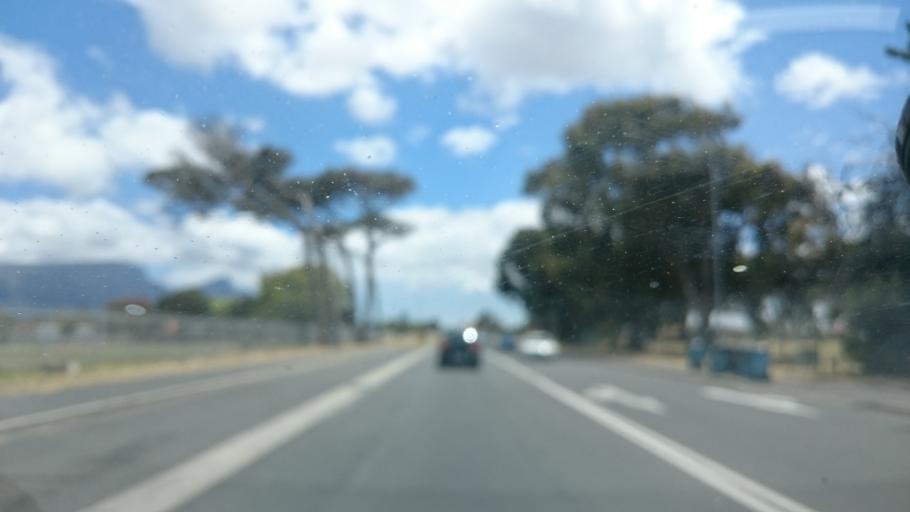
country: ZA
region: Western Cape
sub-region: City of Cape Town
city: Bergvliet
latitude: -34.0595
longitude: 18.4602
